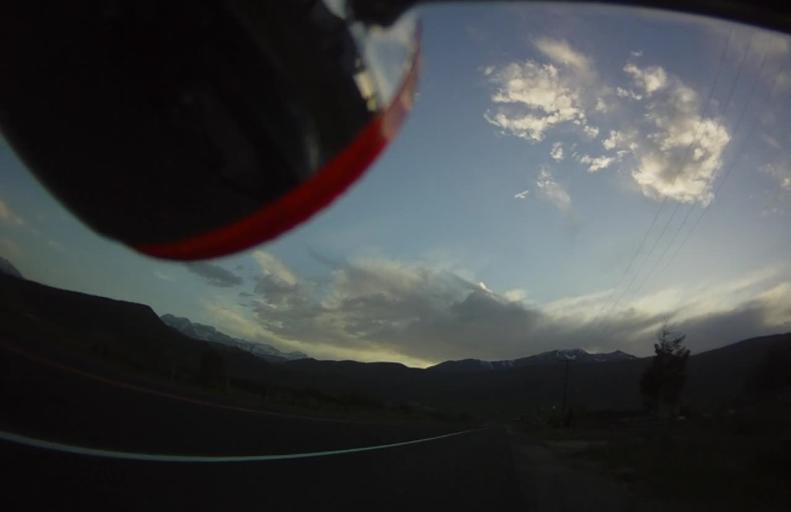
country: US
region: Utah
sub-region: Wasatch County
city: Midway
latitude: 40.4867
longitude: -111.4751
